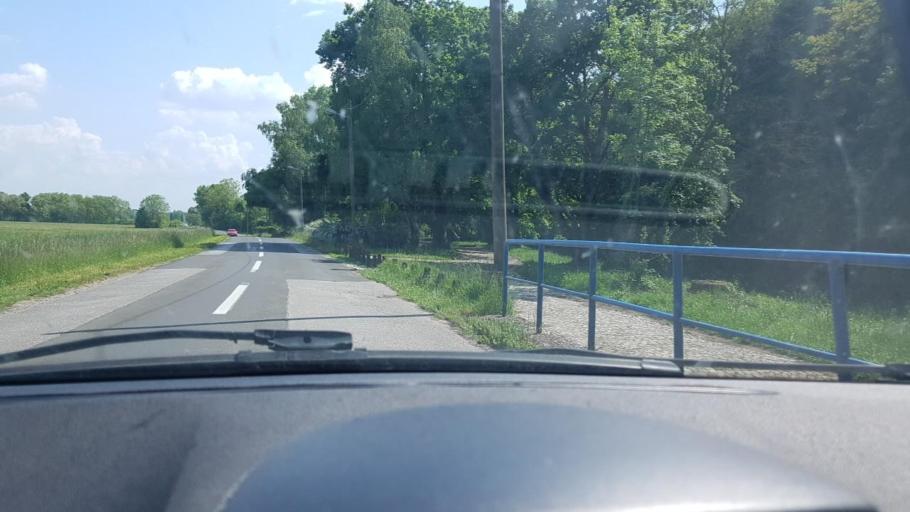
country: HR
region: Grad Zagreb
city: Dubrava
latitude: 45.8338
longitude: 16.0291
